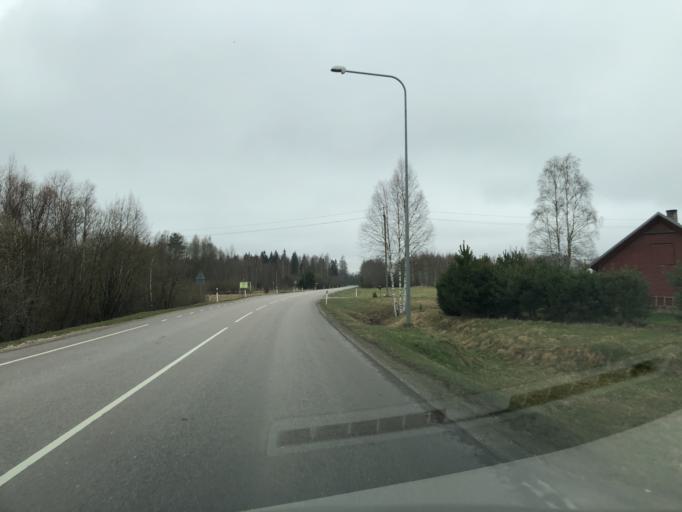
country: EE
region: Laeaene-Virumaa
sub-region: Rakke vald
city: Rakke
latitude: 58.9870
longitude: 26.2612
